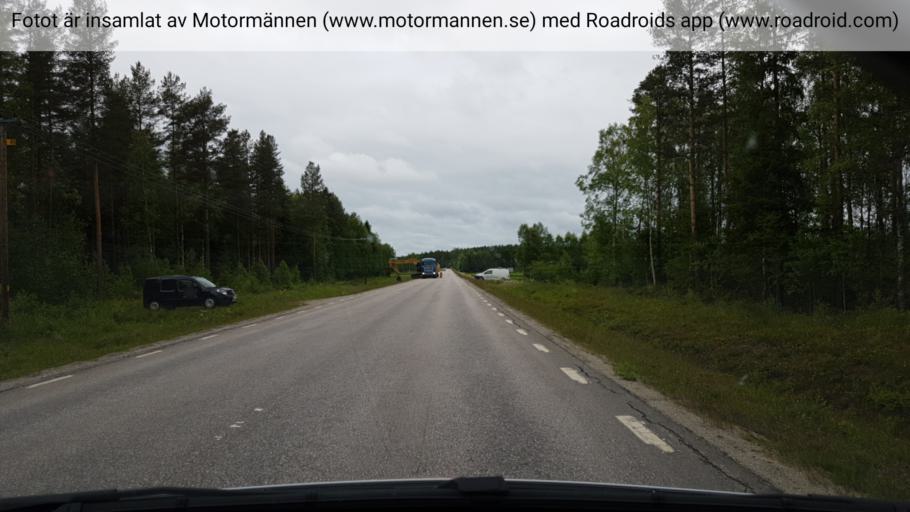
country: SE
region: Vaesterbotten
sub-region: Vindelns Kommun
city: Vindeln
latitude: 64.0483
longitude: 19.6778
